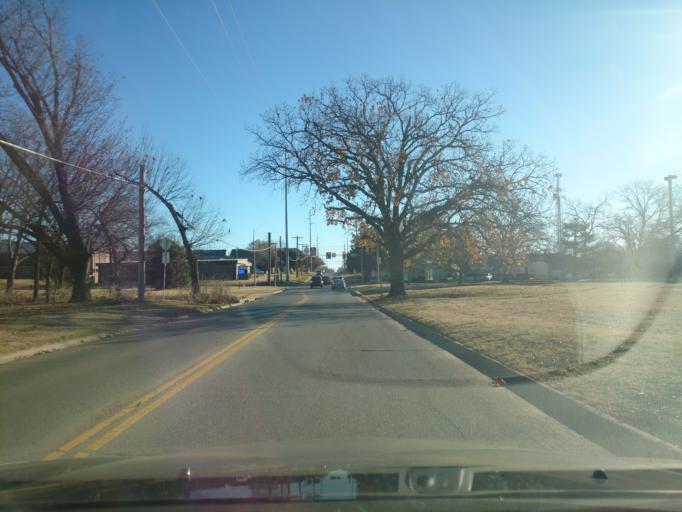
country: US
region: Oklahoma
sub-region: Payne County
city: Stillwater
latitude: 36.1305
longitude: -97.0638
